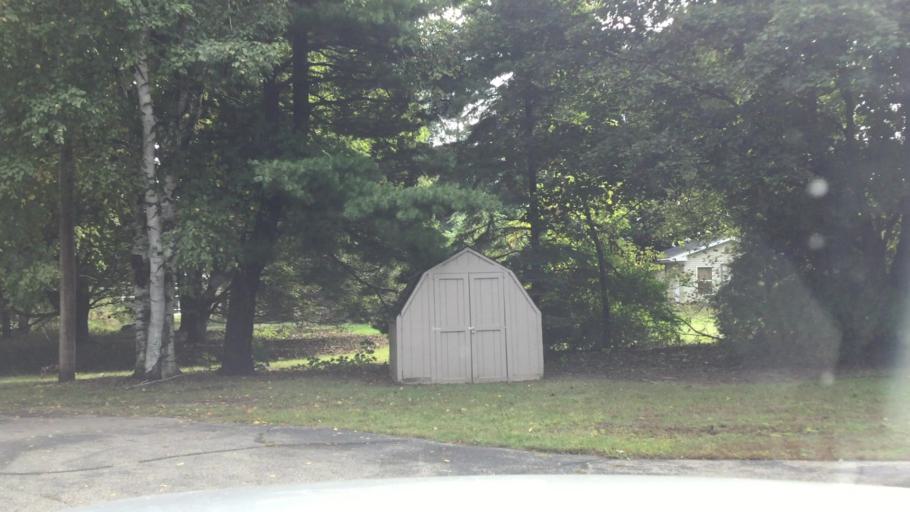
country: US
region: Michigan
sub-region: Shiawassee County
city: Perry
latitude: 42.8335
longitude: -84.2155
